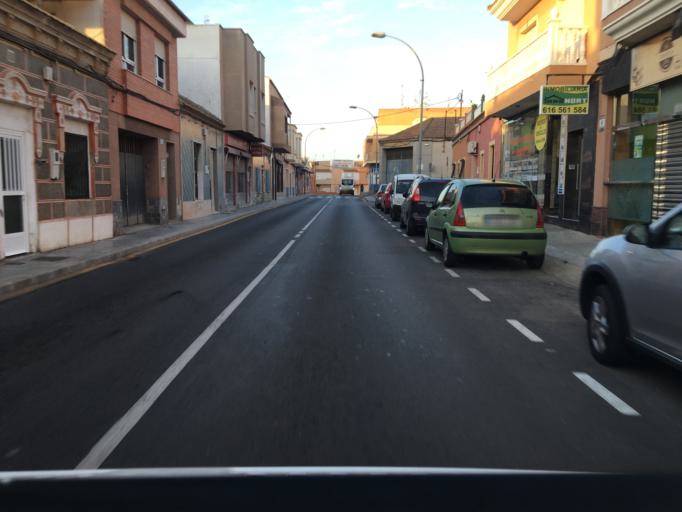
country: ES
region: Murcia
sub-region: Murcia
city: Cartagena
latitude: 37.6285
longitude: -0.9875
